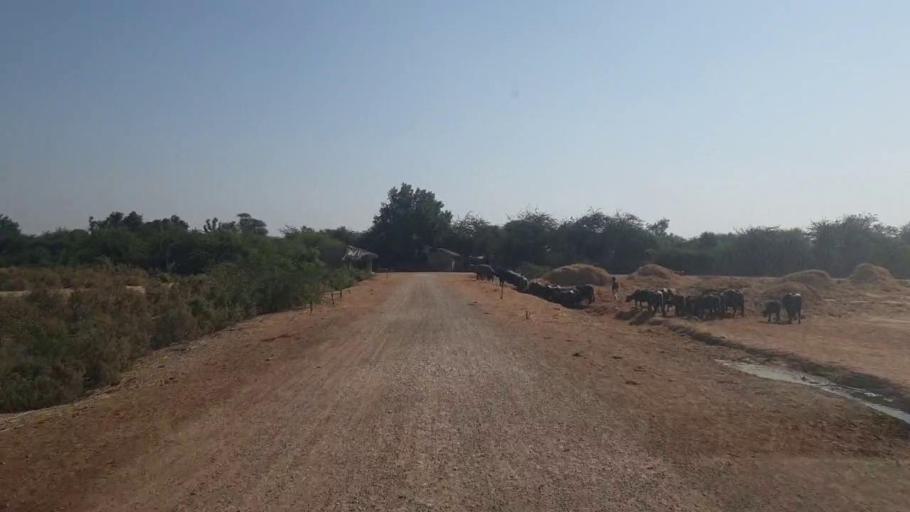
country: PK
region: Sindh
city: Badin
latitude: 24.5518
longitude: 68.8473
